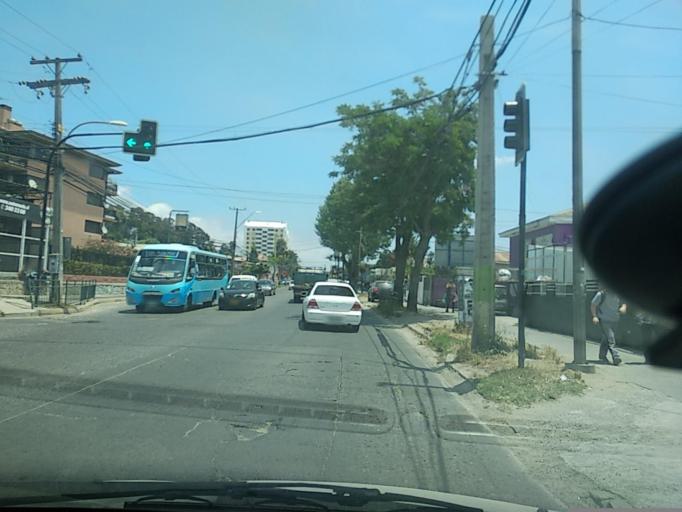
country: CL
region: Valparaiso
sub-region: Provincia de Marga Marga
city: Quilpue
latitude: -33.0471
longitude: -71.4491
